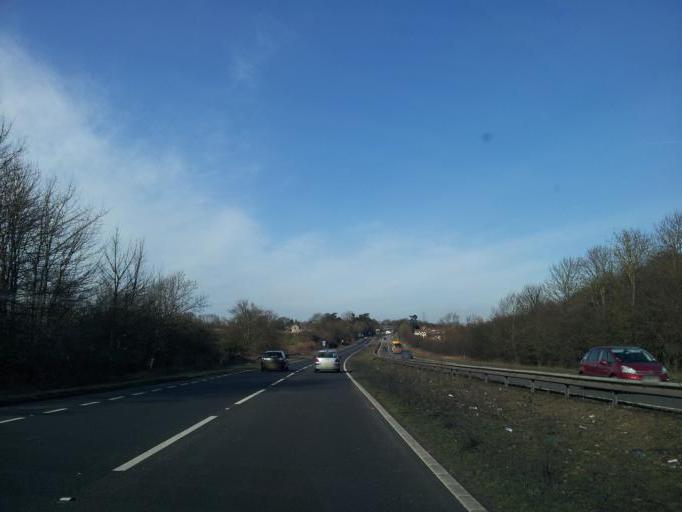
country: GB
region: England
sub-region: Lincolnshire
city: Grantham
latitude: 52.8550
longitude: -0.6281
